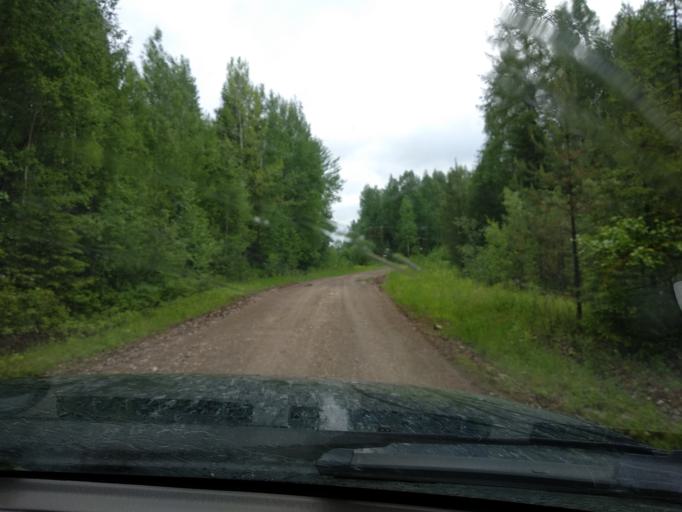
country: RU
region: Sverdlovsk
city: Karpinsk
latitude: 59.4418
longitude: 59.9724
